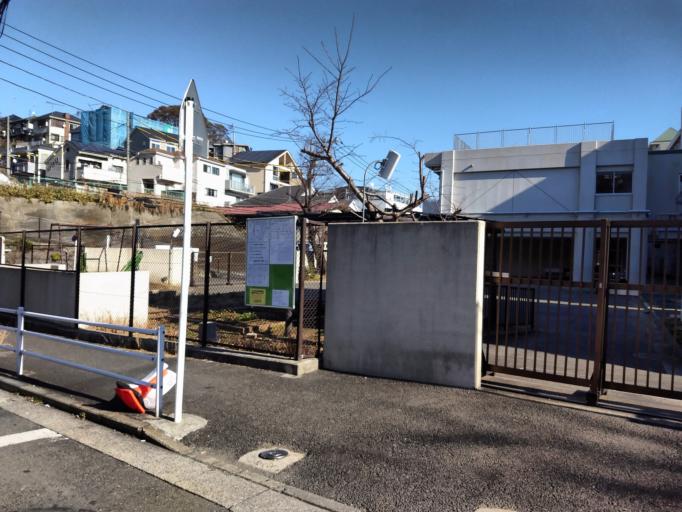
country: JP
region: Kanagawa
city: Yokohama
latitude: 35.4270
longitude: 139.6444
